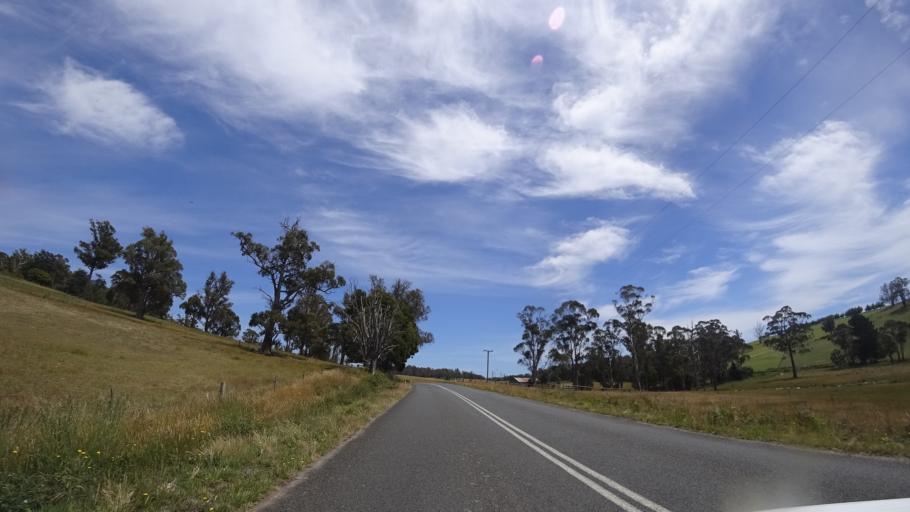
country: AU
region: Tasmania
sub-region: Dorset
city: Scottsdale
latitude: -41.1613
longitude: 147.4536
